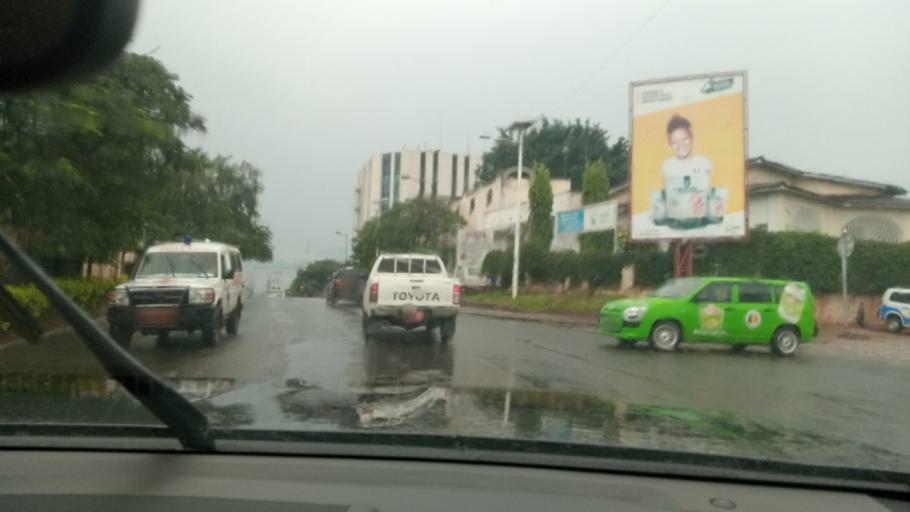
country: BI
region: Bujumbura Mairie
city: Bujumbura
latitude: -3.3815
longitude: 29.3595
